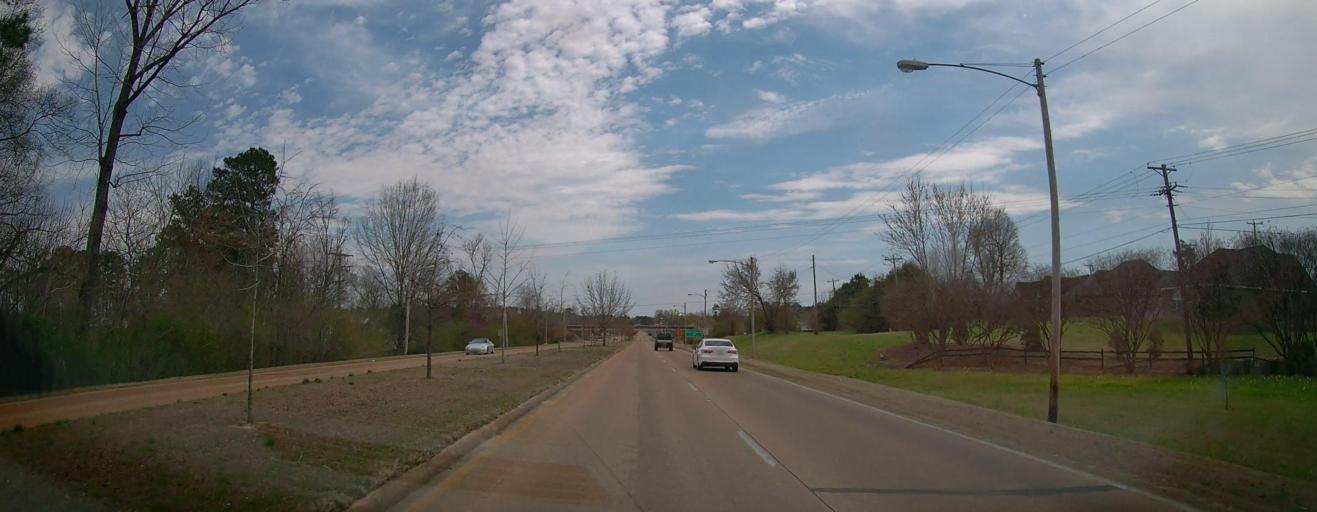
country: US
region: Mississippi
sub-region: Lee County
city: Tupelo
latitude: 34.2800
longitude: -88.7286
